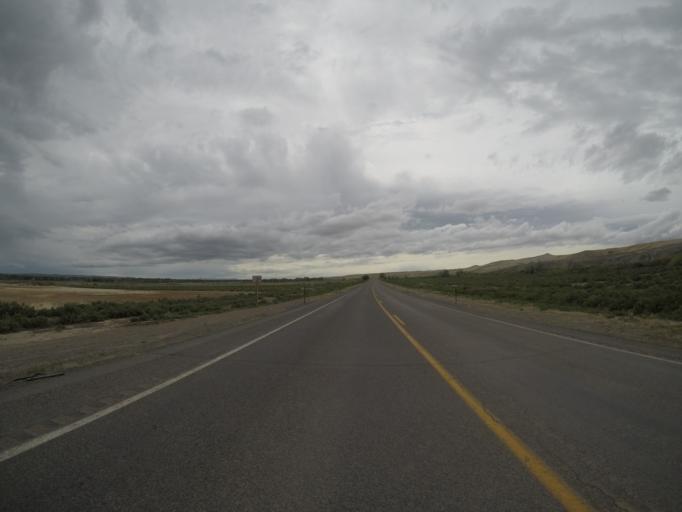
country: US
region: Wyoming
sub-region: Big Horn County
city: Lovell
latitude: 44.8782
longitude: -108.2934
